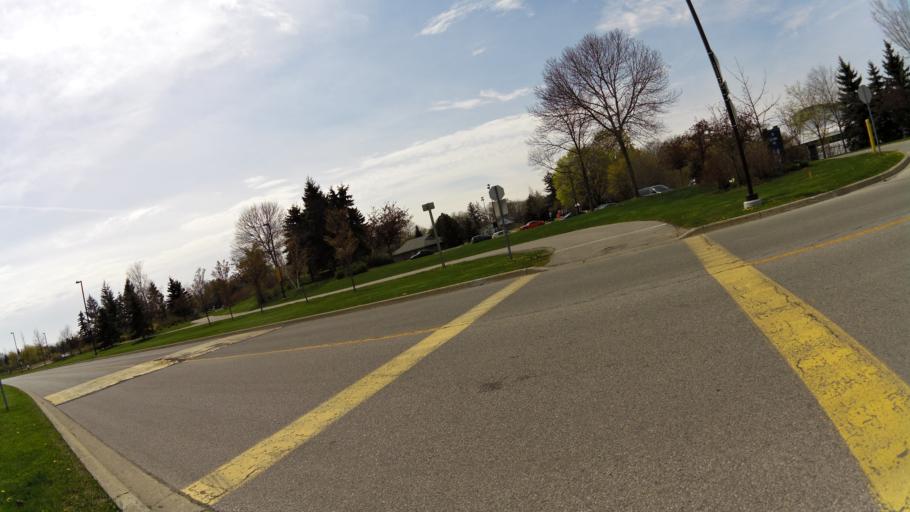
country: CA
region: Ontario
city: Etobicoke
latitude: 43.5684
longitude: -79.5602
